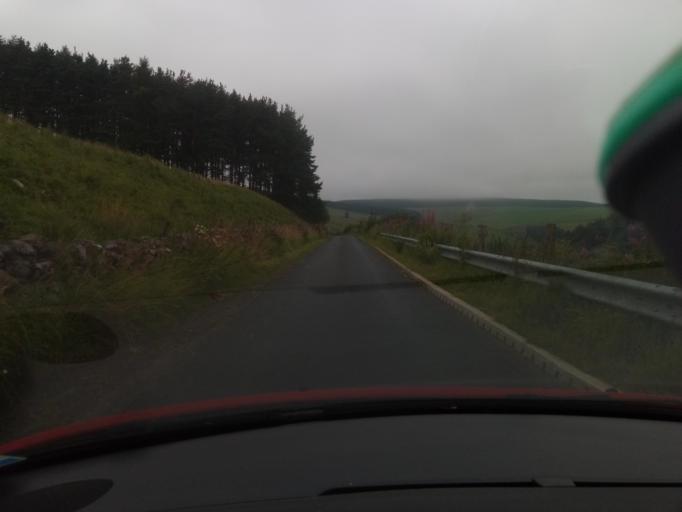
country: GB
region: Scotland
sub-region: The Scottish Borders
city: Galashiels
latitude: 55.6983
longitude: -2.8825
